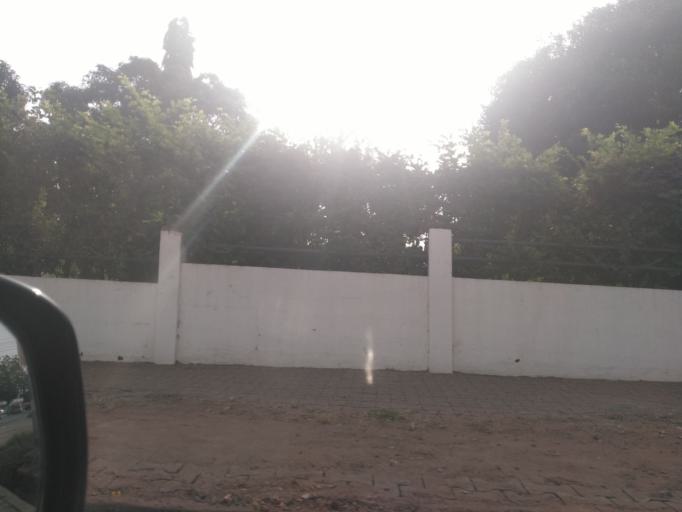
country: GH
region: Greater Accra
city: Accra
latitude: 5.6002
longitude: -0.1939
